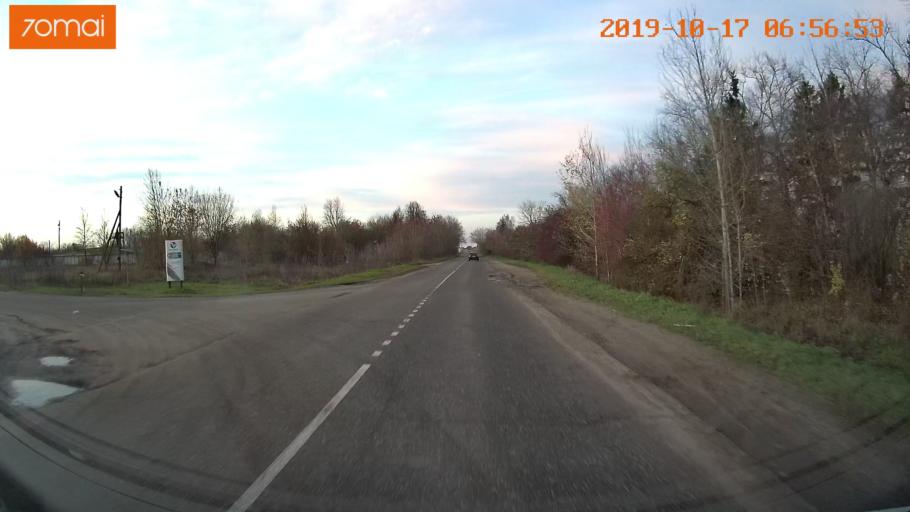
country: RU
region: Vladimir
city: Suzdal'
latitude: 56.4417
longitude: 40.4437
